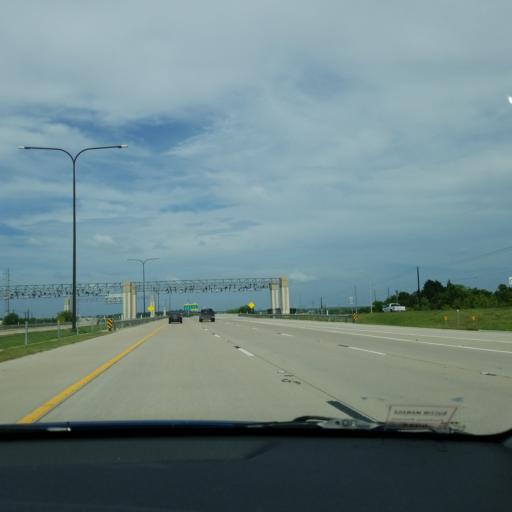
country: US
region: Texas
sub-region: Travis County
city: Manor
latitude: 30.3305
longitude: -97.6266
